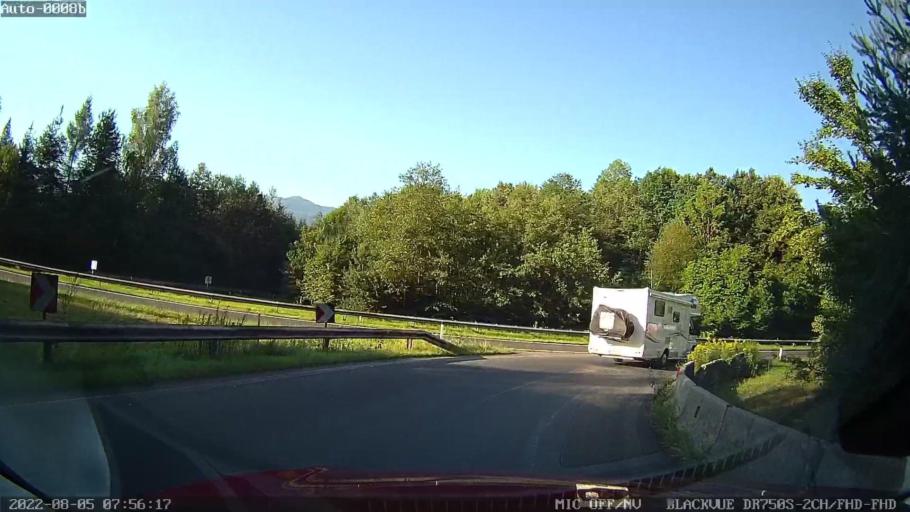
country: AT
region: Carinthia
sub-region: Politischer Bezirk Villach Land
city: Finkenstein am Faaker See
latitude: 46.5736
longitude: 13.8239
